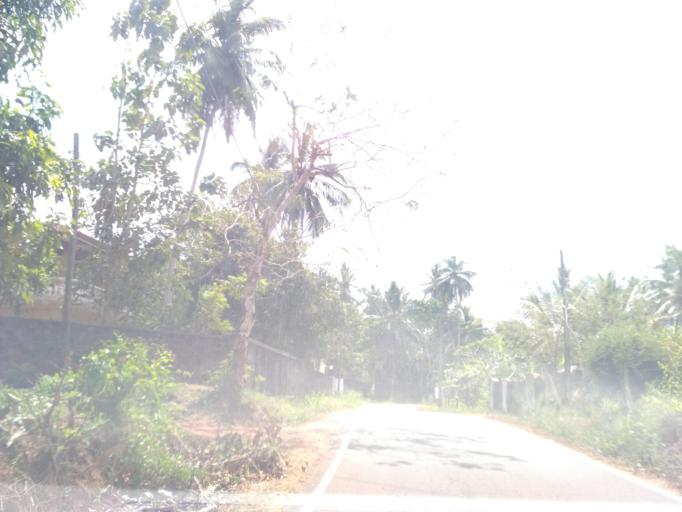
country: LK
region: North Western
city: Kuliyapitiya
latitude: 7.3303
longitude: 80.0632
